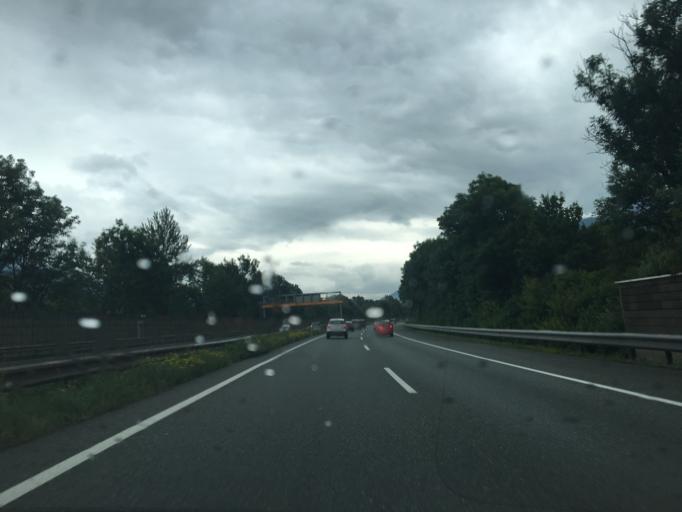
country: AT
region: Tyrol
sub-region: Politischer Bezirk Schwaz
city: Terfens
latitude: 47.3140
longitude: 11.6400
